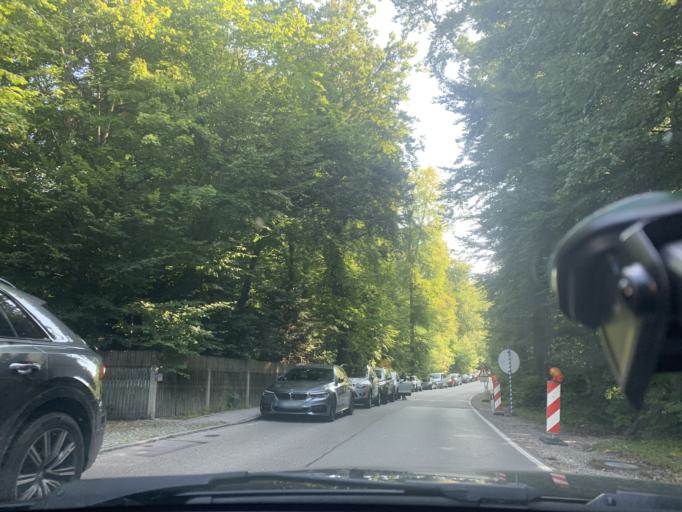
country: DE
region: Bavaria
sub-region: Upper Bavaria
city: Feldafing
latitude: 47.9528
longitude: 11.3026
